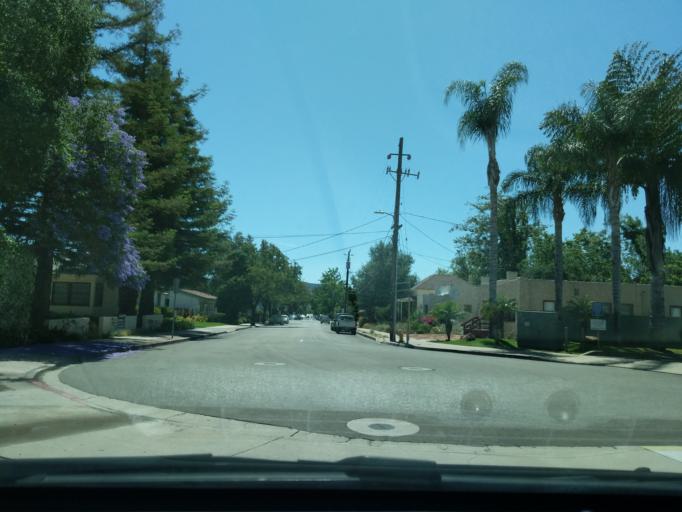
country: US
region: California
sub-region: San Luis Obispo County
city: San Luis Obispo
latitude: 35.2812
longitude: -120.6569
